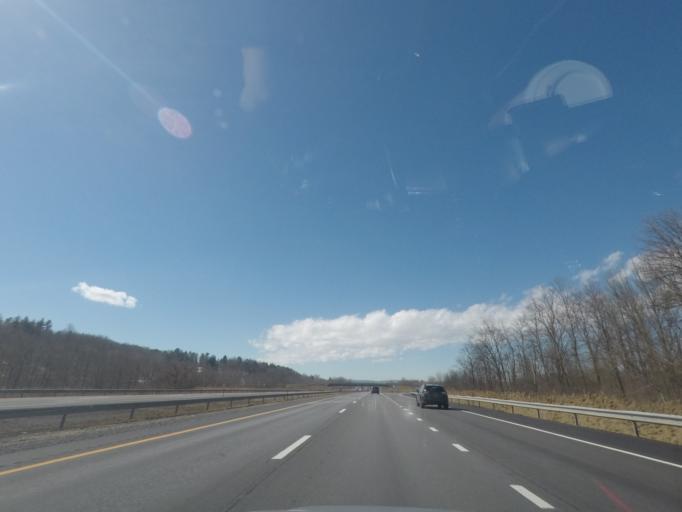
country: US
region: New York
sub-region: Montgomery County
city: Fonda
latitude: 42.9440
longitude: -74.3551
